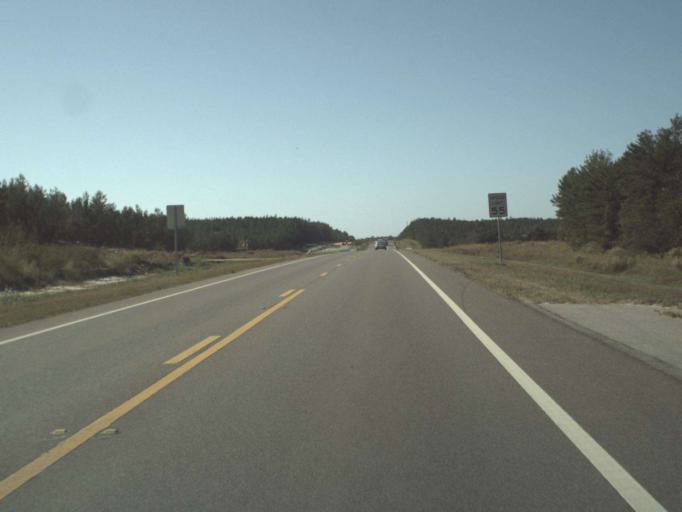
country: US
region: Florida
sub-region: Walton County
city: Freeport
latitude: 30.5143
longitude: -86.1113
